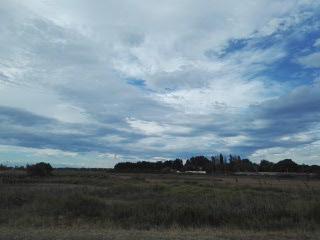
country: FR
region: Languedoc-Roussillon
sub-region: Departement de l'Herault
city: Marseillan
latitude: 43.3144
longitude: 3.5374
